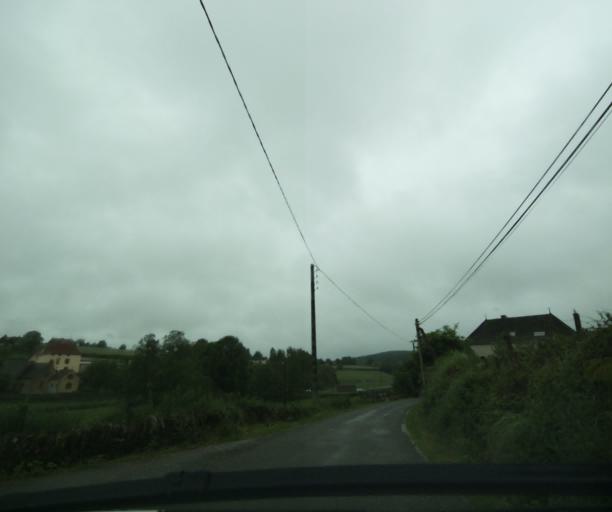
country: FR
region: Bourgogne
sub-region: Departement de Saone-et-Loire
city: Charolles
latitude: 46.4017
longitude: 4.2652
